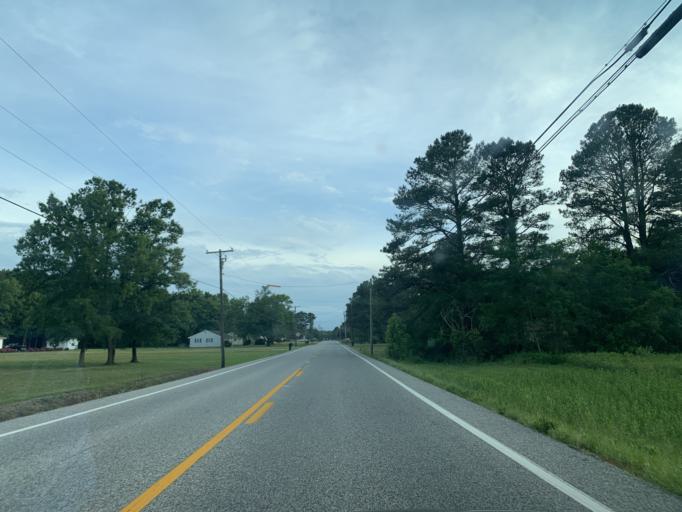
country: US
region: Maryland
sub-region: Worcester County
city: Snow Hill
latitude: 38.1503
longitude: -75.4100
